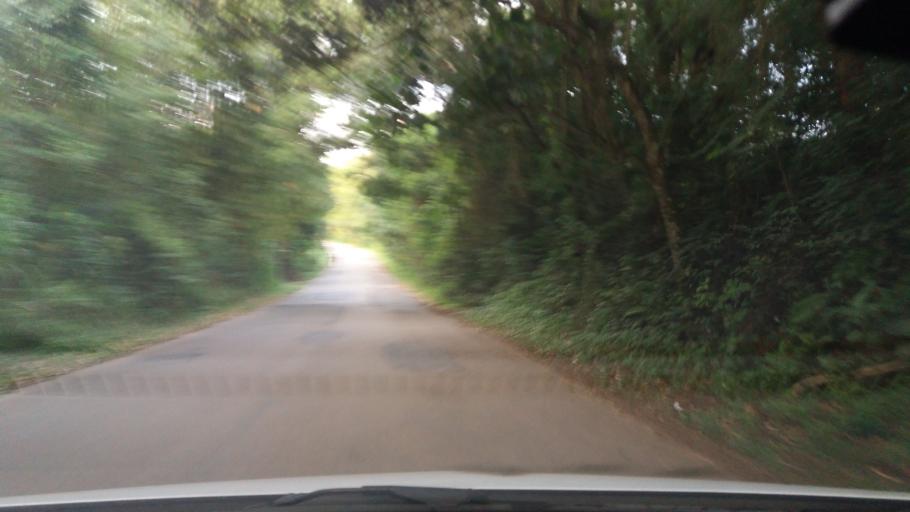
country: BR
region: Sao Paulo
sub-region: Bom Jesus Dos Perdoes
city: Bom Jesus dos Perdoes
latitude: -23.1670
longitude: -46.4779
